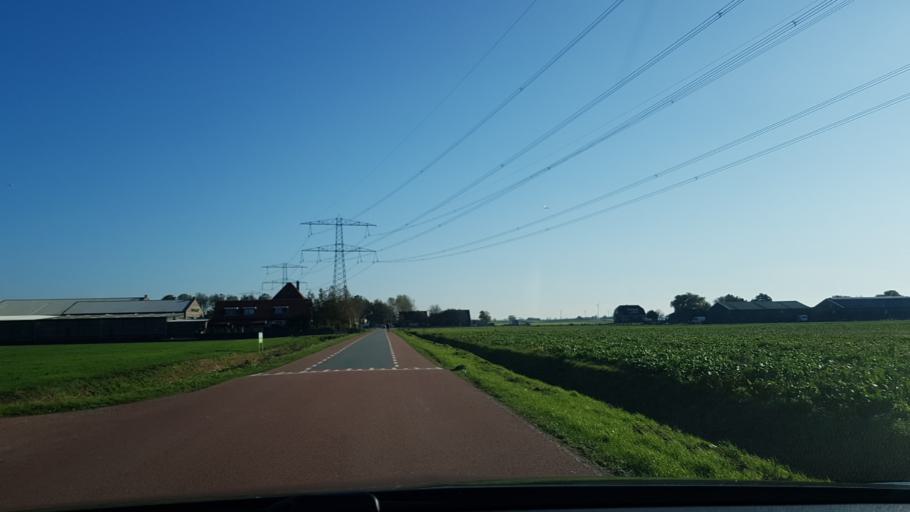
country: NL
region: North Holland
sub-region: Gemeente Beverwijk
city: Beverwijk
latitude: 52.4704
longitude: 4.6909
